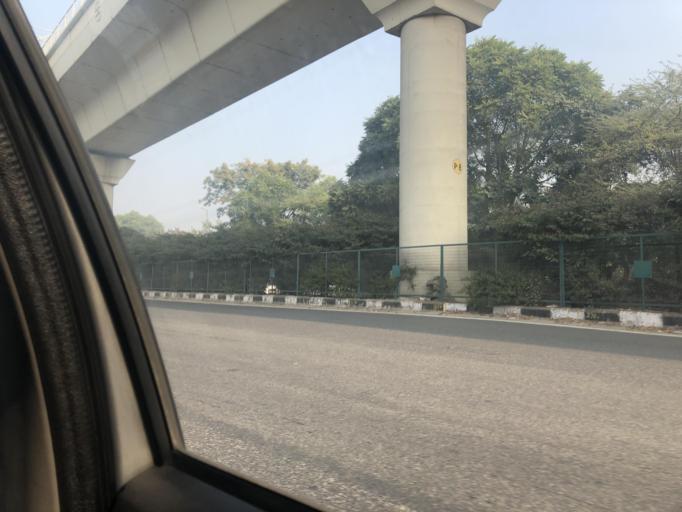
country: IN
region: NCT
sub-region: Central Delhi
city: Karol Bagh
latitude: 28.6097
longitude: 77.1395
